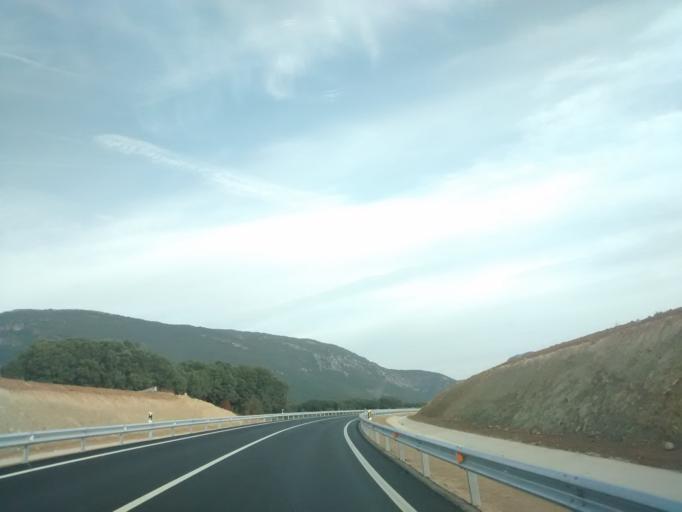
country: ES
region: Aragon
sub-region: Provincia de Zaragoza
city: Siguees
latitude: 42.6189
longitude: -1.0399
